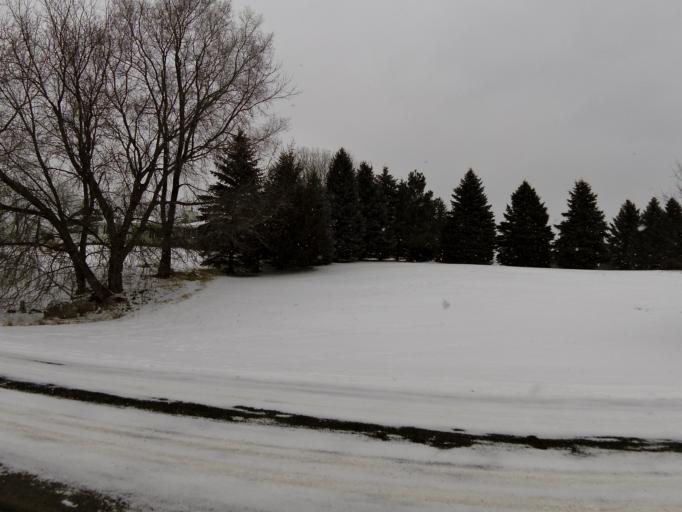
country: US
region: Minnesota
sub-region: Washington County
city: Lake Elmo
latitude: 44.9749
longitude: -92.8436
